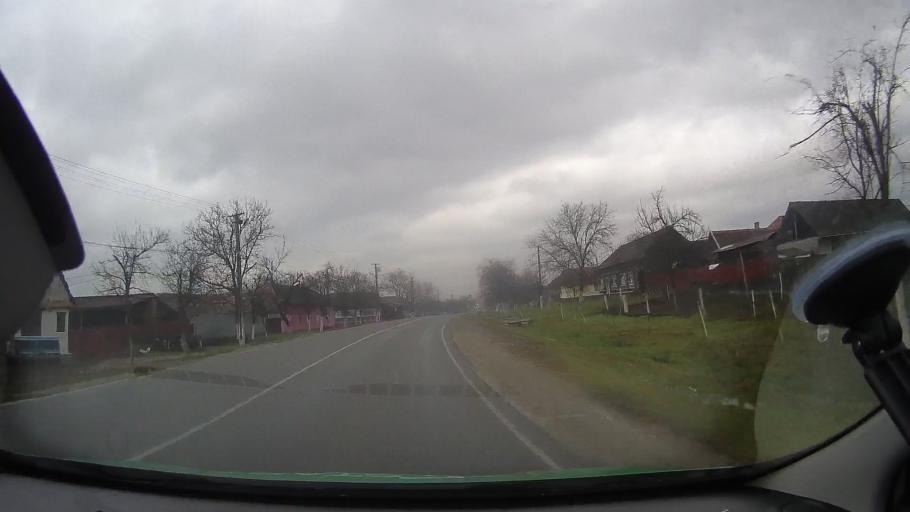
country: RO
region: Arad
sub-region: Comuna Almas
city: Almas
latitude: 46.2901
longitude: 22.2237
